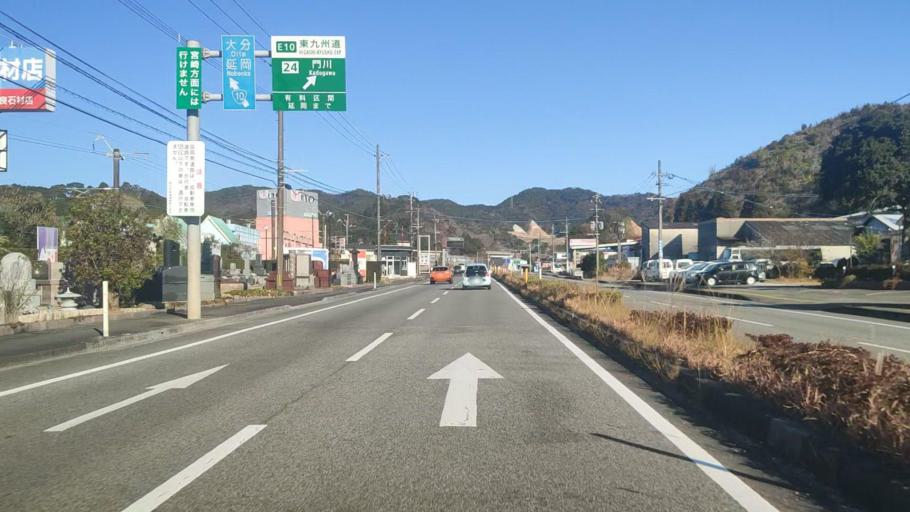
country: JP
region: Miyazaki
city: Nobeoka
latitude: 32.4932
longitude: 131.6631
